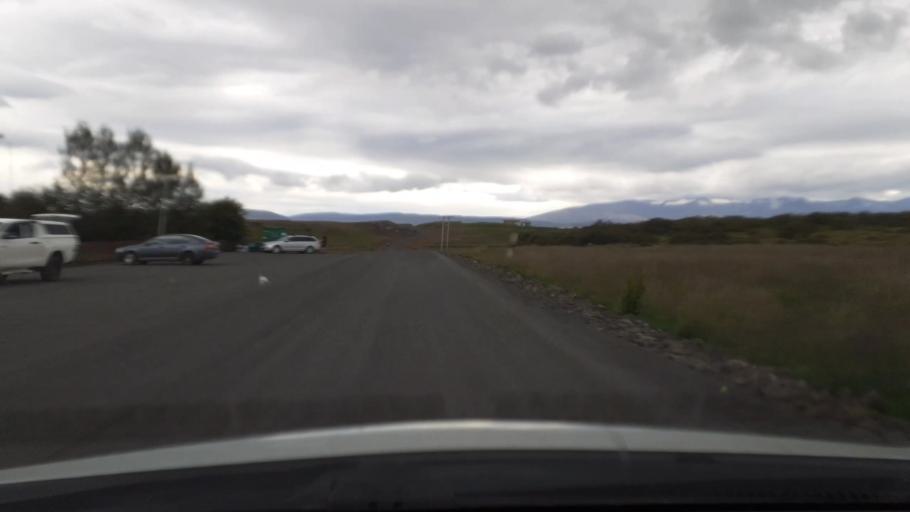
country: IS
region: West
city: Borgarnes
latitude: 64.6743
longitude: -21.7061
